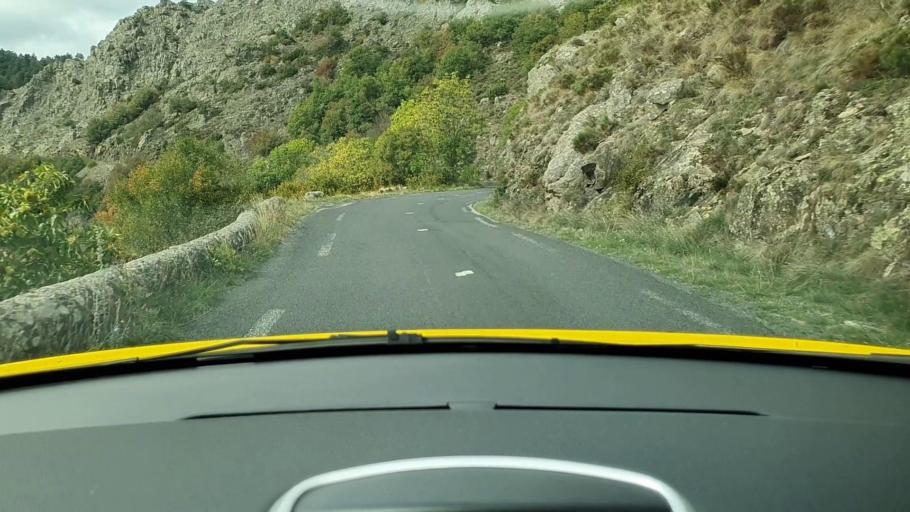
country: FR
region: Languedoc-Roussillon
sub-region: Departement de la Lozere
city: Meyrueis
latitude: 44.0672
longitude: 3.4189
